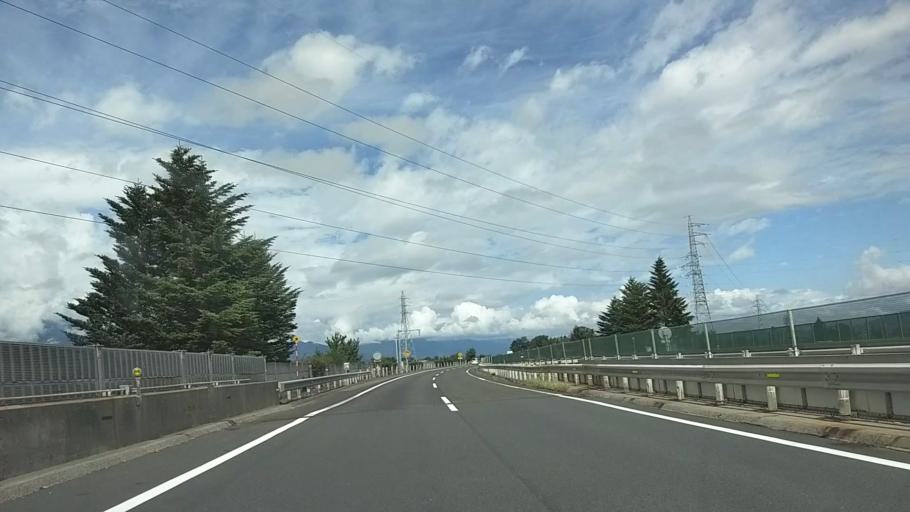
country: JP
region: Nagano
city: Matsumoto
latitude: 36.2034
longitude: 137.9317
